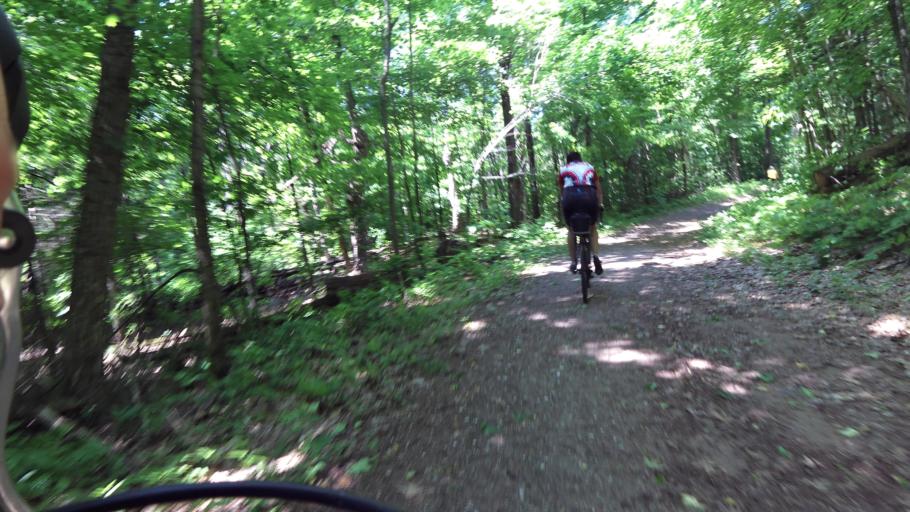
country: CA
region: Quebec
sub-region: Outaouais
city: Wakefield
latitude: 45.5664
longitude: -75.9106
